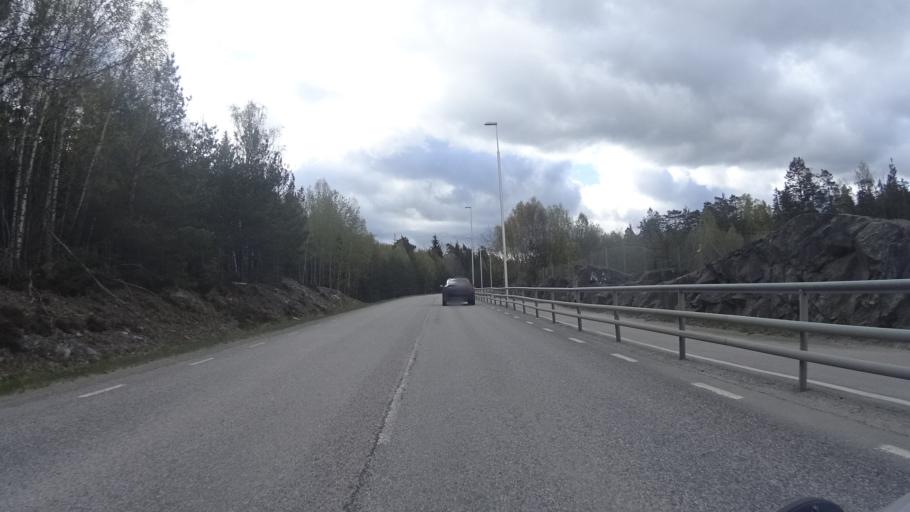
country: SE
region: Stockholm
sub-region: Botkyrka Kommun
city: Tullinge
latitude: 59.2005
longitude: 17.9269
